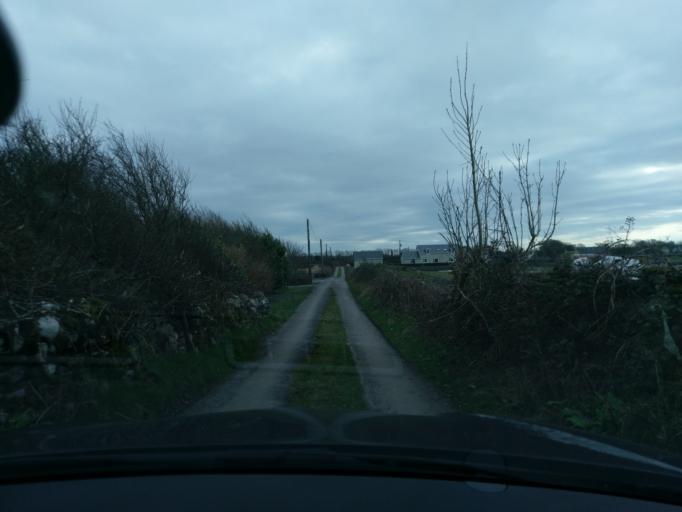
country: IE
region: Connaught
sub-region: County Galway
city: Oranmore
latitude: 53.2033
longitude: -8.9224
